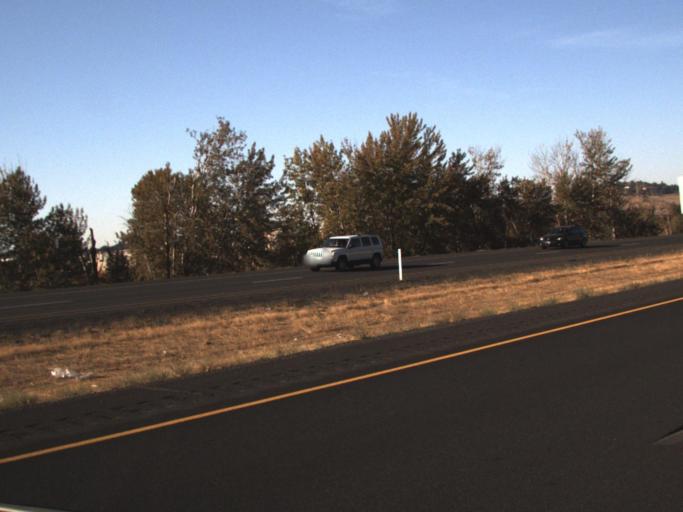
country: US
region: Washington
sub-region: Yakima County
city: Selah
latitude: 46.6227
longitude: -120.5409
